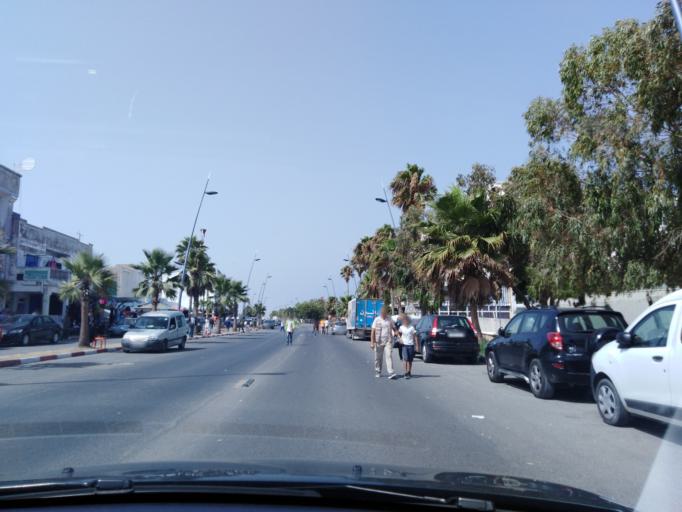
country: MA
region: Doukkala-Abda
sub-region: Safi
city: Safi
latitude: 32.7353
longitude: -9.0321
